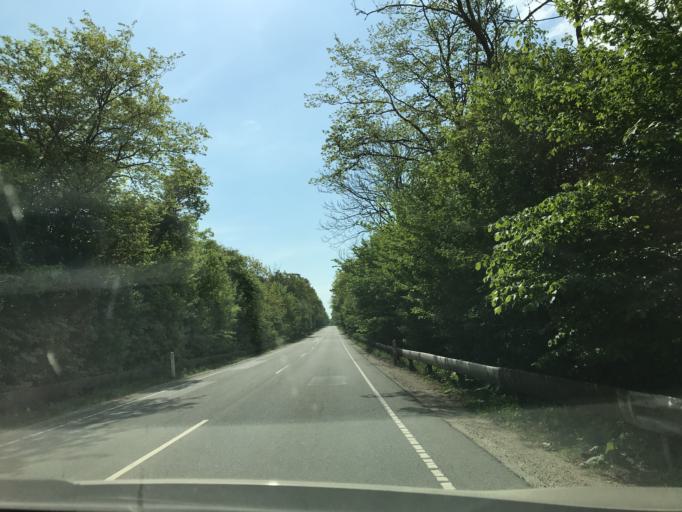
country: DK
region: South Denmark
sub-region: Middelfart Kommune
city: Ejby
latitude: 55.3970
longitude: 9.9054
